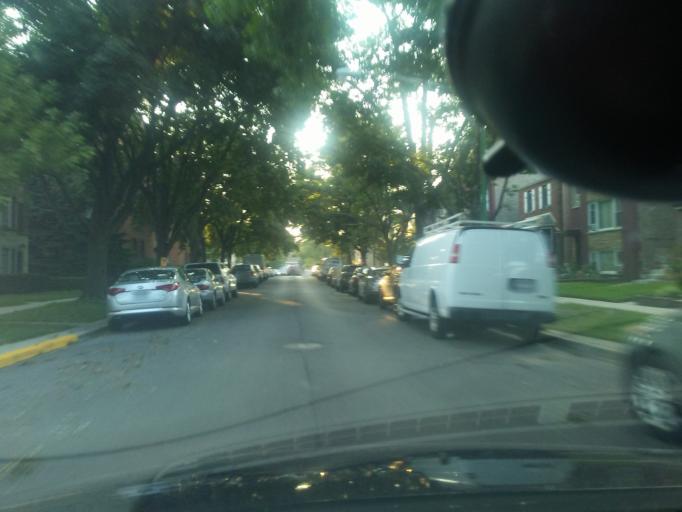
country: US
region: Illinois
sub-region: Cook County
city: Lincolnwood
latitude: 41.9804
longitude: -87.6955
